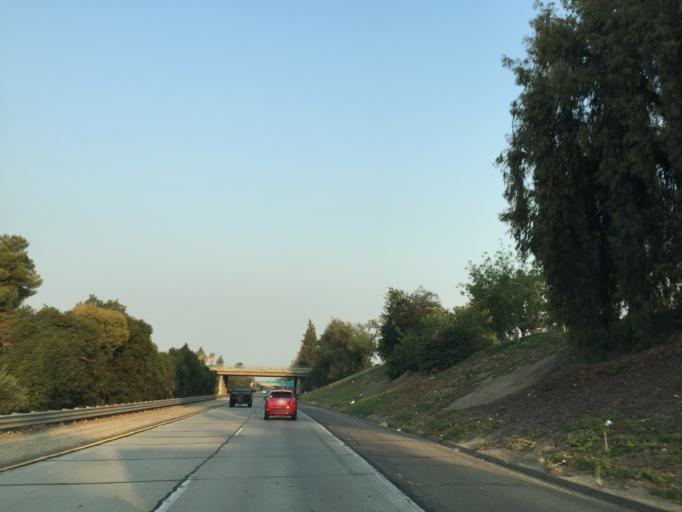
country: US
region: California
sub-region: Tulare County
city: Visalia
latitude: 36.3270
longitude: -119.2814
